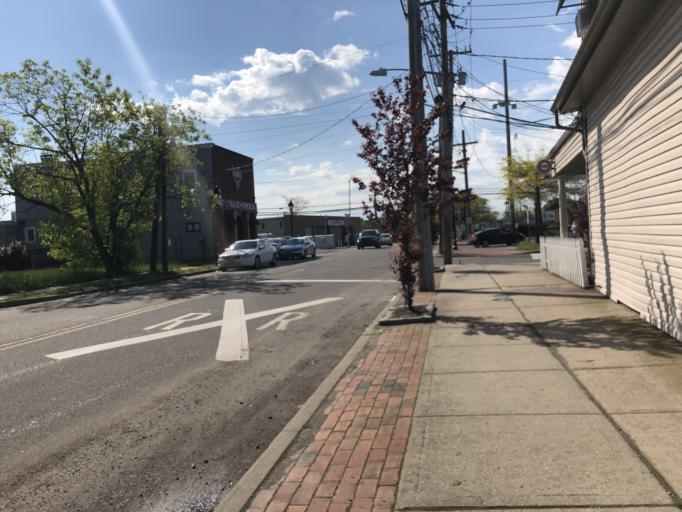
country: US
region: New York
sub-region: Suffolk County
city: Bay Shore
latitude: 40.7258
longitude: -73.2529
